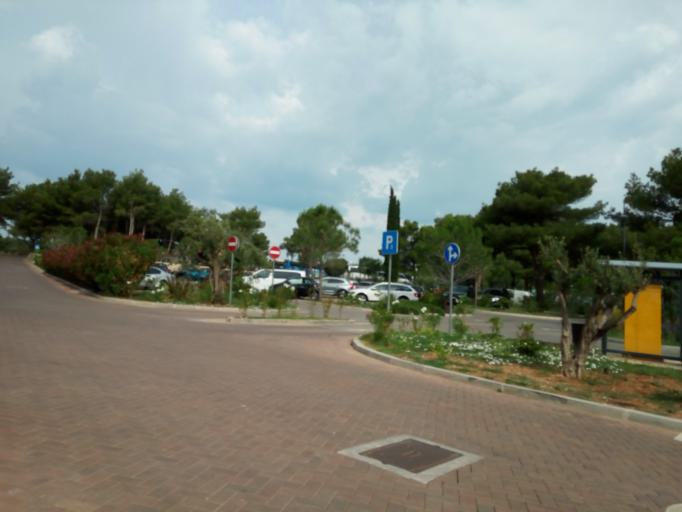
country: HR
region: Sibensko-Kniniska
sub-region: Grad Sibenik
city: Sibenik
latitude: 43.6968
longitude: 15.8881
